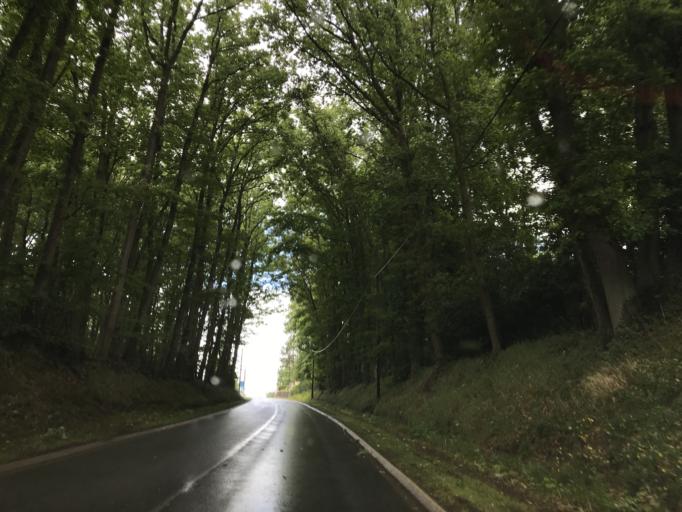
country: FR
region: Haute-Normandie
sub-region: Departement de l'Eure
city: Damville
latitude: 48.8735
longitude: 1.0670
